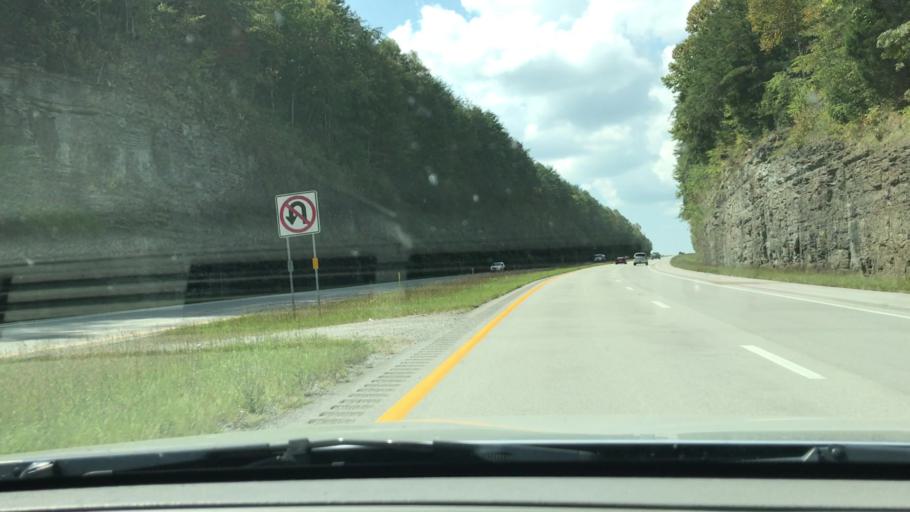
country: US
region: Kentucky
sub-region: Russell County
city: Russell Springs
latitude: 37.0864
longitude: -84.8921
